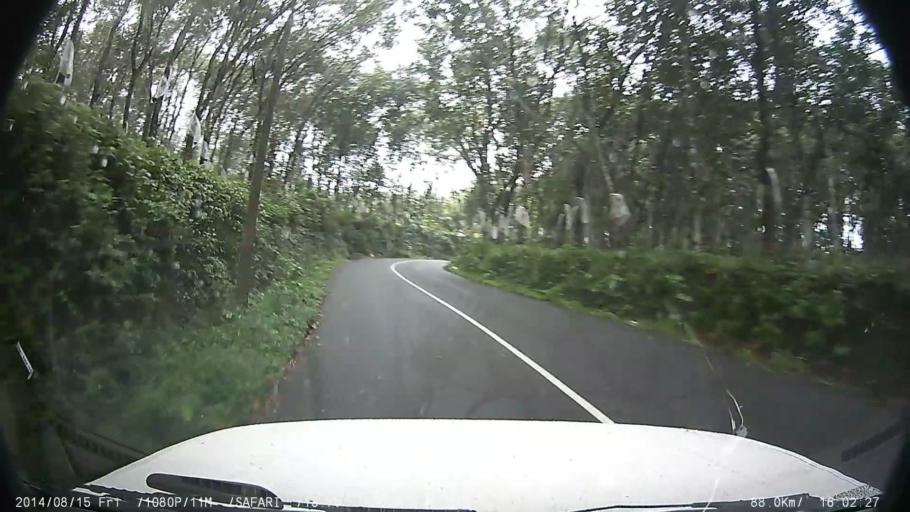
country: IN
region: Kerala
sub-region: Kottayam
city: Lalam
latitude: 9.7698
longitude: 76.7092
